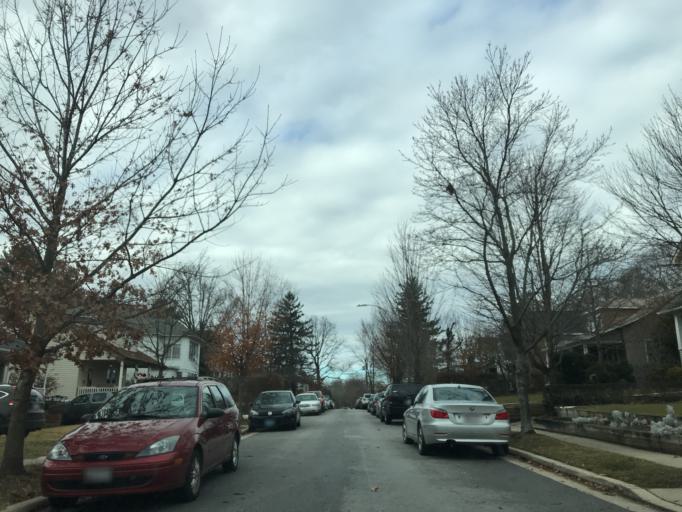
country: US
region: Maryland
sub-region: Baltimore County
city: Towson
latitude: 39.3773
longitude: -76.6065
